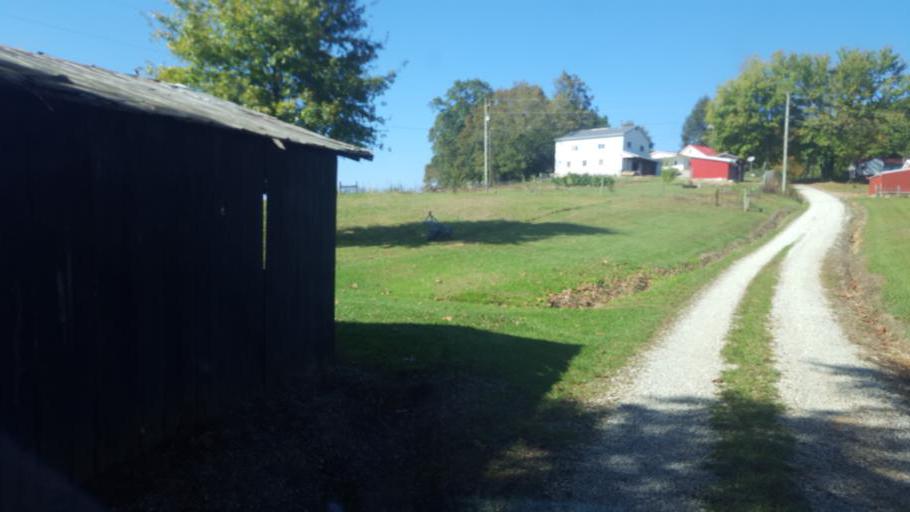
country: US
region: Kentucky
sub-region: Fleming County
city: Flemingsburg
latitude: 38.4649
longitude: -83.5725
